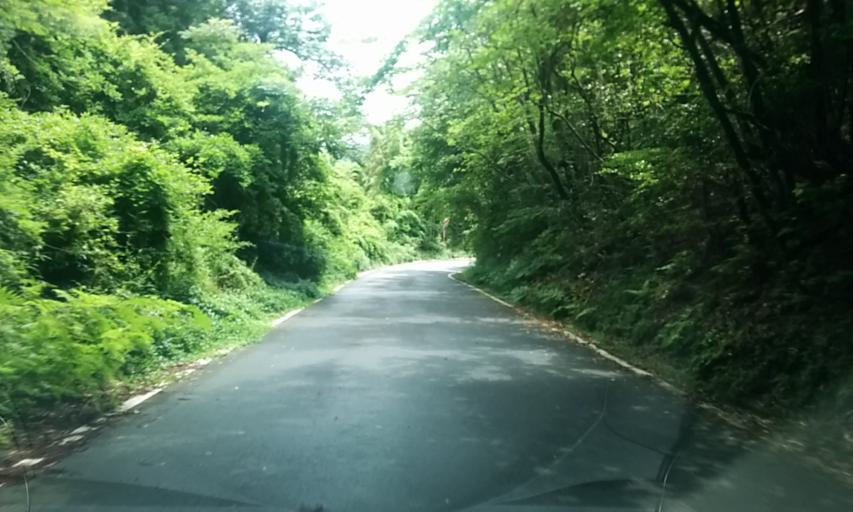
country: JP
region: Kyoto
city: Kameoka
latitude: 35.0892
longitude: 135.4520
